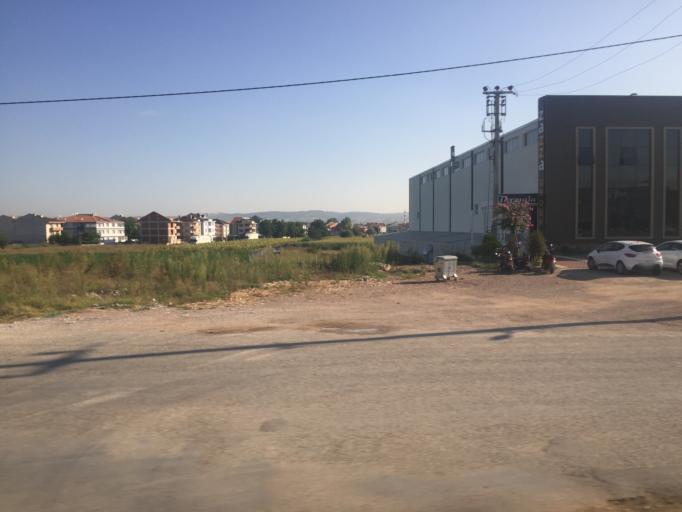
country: TR
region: Bursa
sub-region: Inegoel
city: Inegol
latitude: 40.0755
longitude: 29.5324
